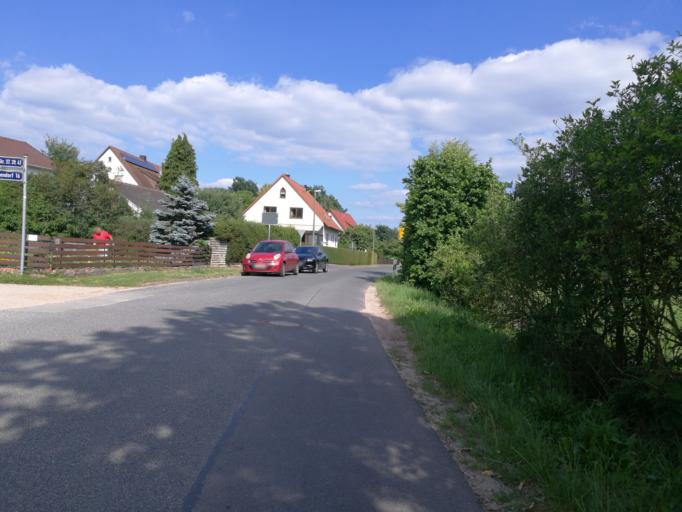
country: DE
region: Bavaria
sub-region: Regierungsbezirk Mittelfranken
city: Veitsbronn
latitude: 49.5088
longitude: 10.8997
